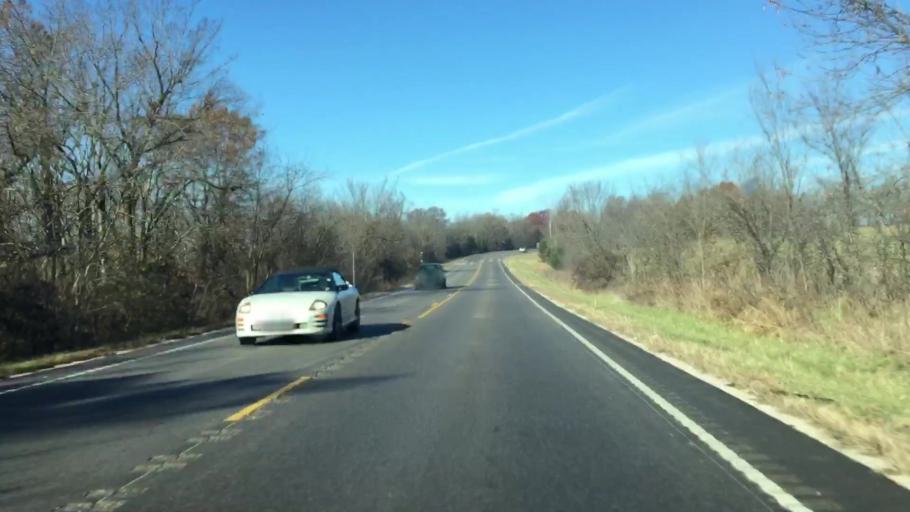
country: US
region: Missouri
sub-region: Miller County
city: Eldon
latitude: 38.3637
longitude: -92.6112
